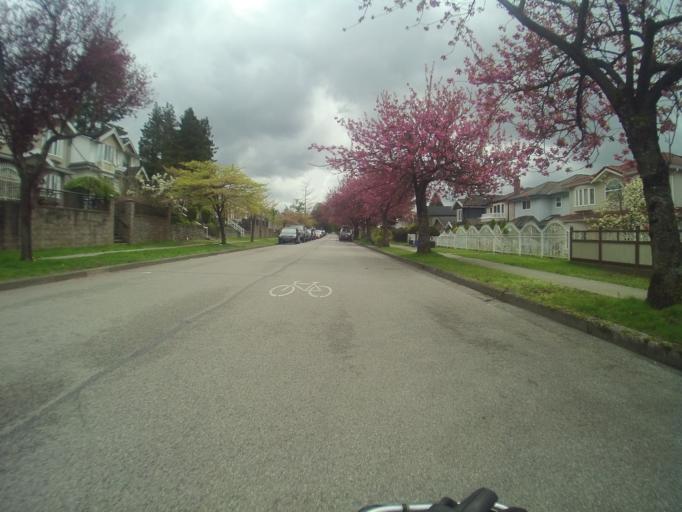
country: CA
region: British Columbia
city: Vancouver
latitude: 49.2289
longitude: -123.0744
